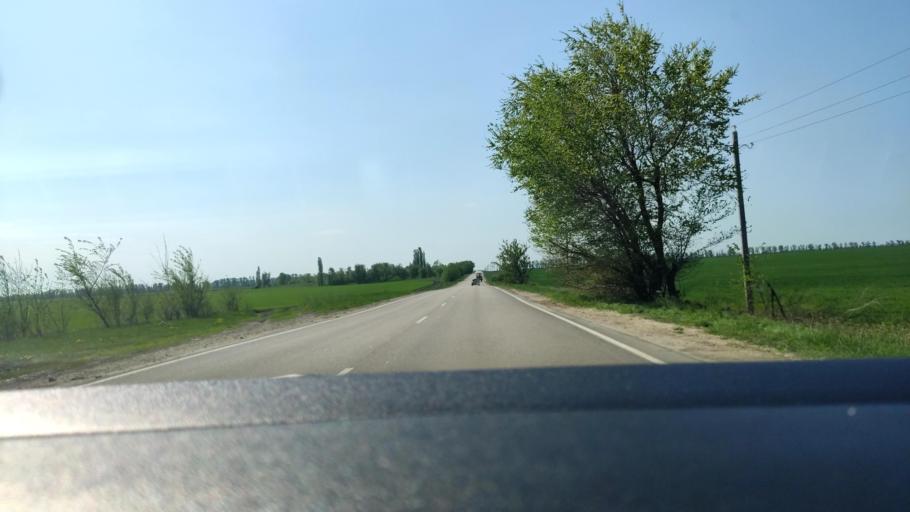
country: RU
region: Voronezj
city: Novaya Usman'
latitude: 51.5775
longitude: 39.3749
